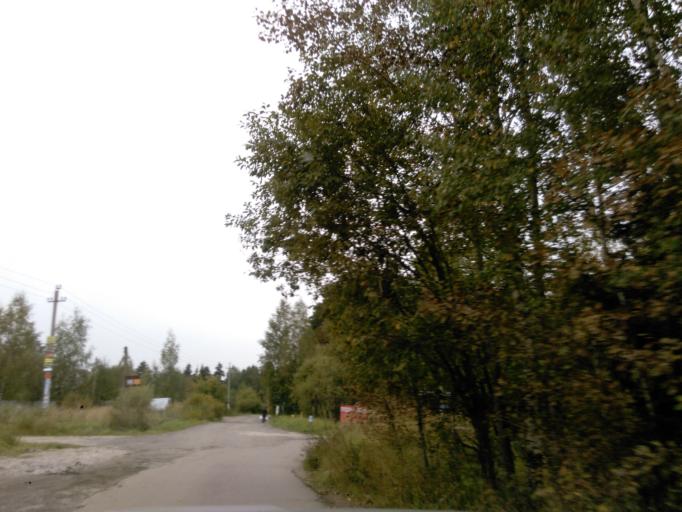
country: RU
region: Moskovskaya
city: Lozhki
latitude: 56.0653
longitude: 37.1075
